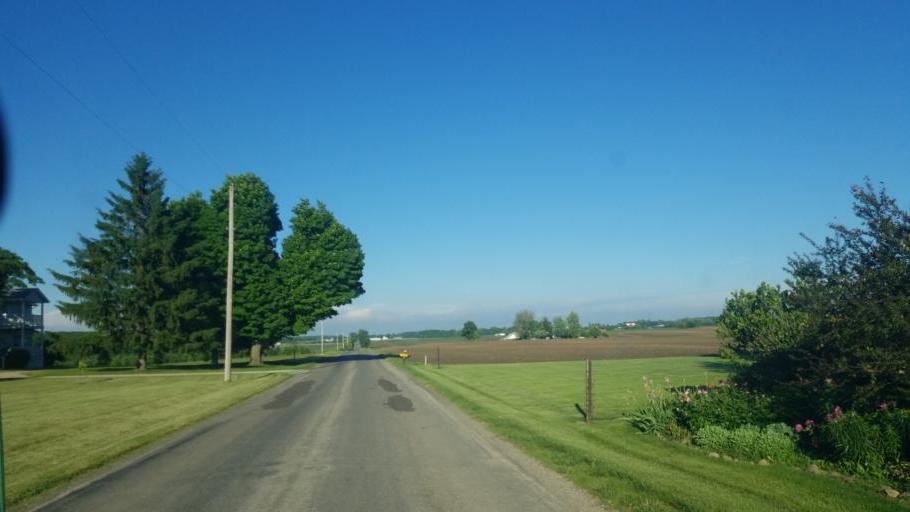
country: US
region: Indiana
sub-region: Marshall County
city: Bremen
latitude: 41.4265
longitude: -86.0971
